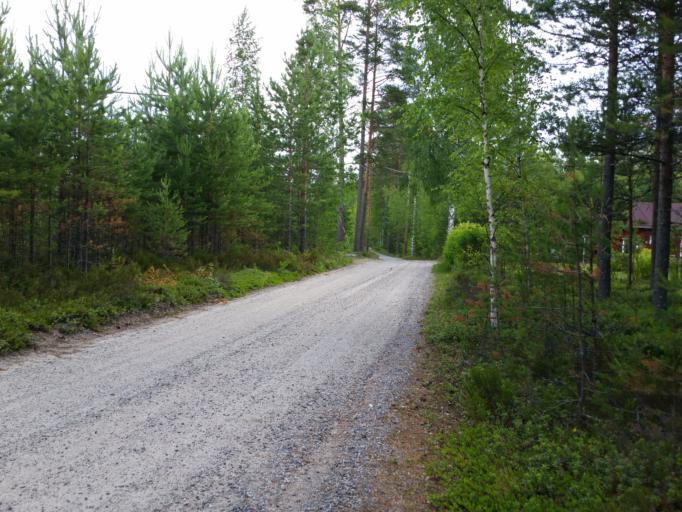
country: FI
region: Southern Savonia
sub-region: Savonlinna
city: Sulkava
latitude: 61.7631
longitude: 28.4352
